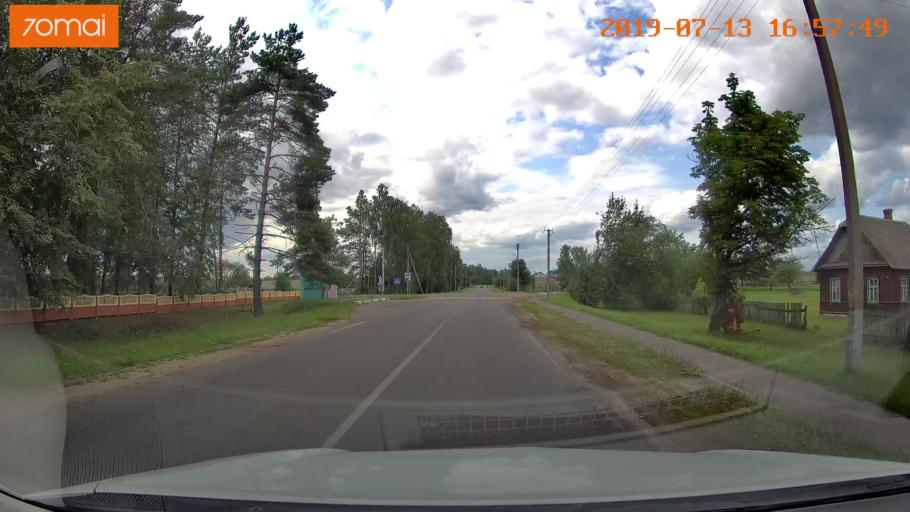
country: BY
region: Mogilev
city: Kirawsk
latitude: 53.2829
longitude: 29.4480
